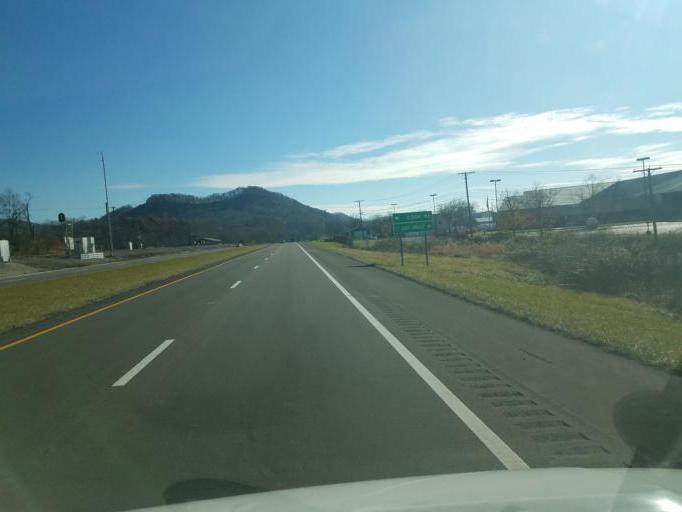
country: US
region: Ohio
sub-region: Scioto County
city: Lucasville
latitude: 38.8616
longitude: -82.9904
